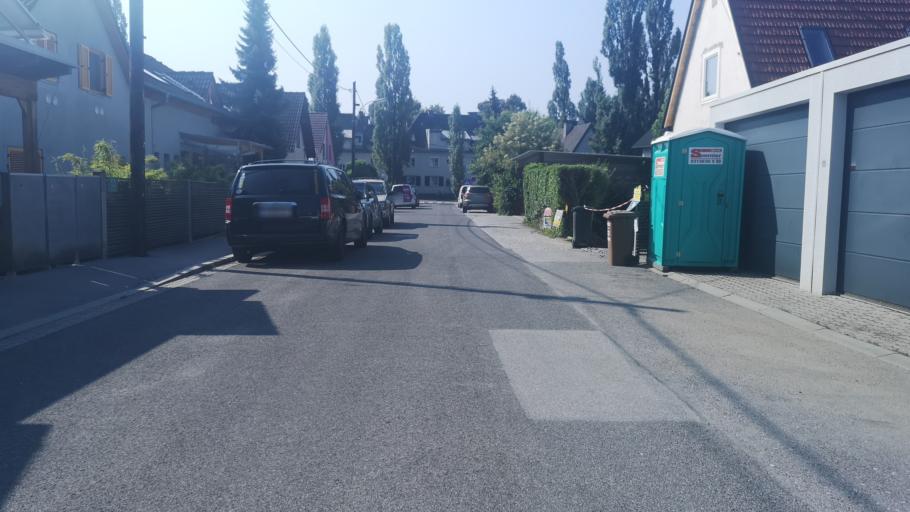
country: AT
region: Styria
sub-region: Graz Stadt
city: Wetzelsdorf
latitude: 47.0519
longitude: 15.4241
